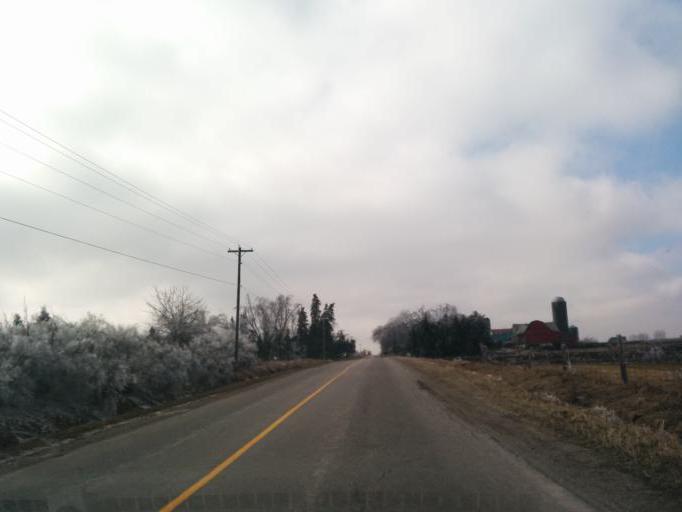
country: CA
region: Ontario
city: Waterloo
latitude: 43.6343
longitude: -80.5644
